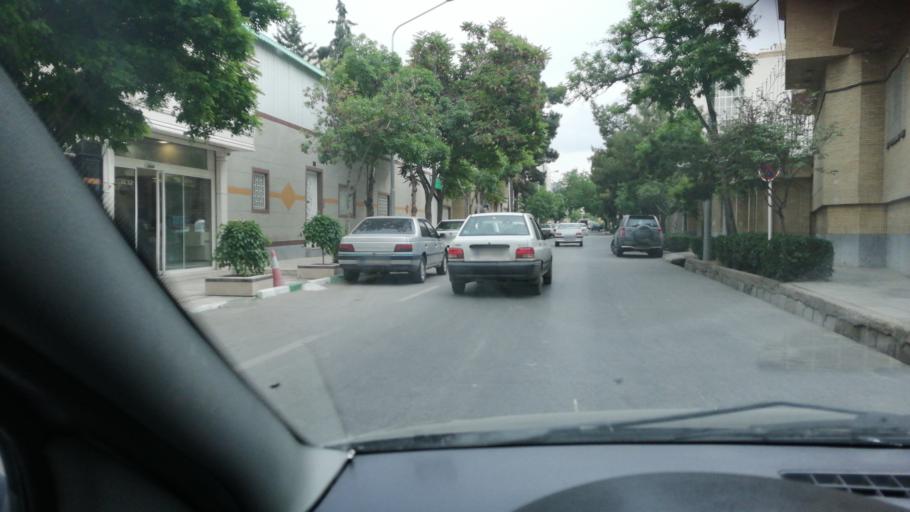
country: IR
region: Razavi Khorasan
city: Mashhad
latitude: 36.2872
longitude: 59.5842
